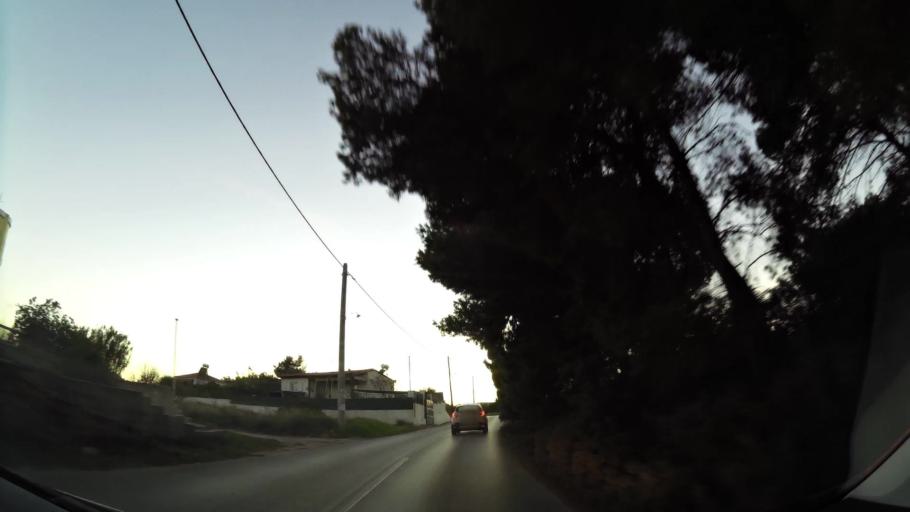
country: GR
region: Attica
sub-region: Nomarchia Anatolikis Attikis
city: Rafina
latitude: 37.9979
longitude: 24.0034
